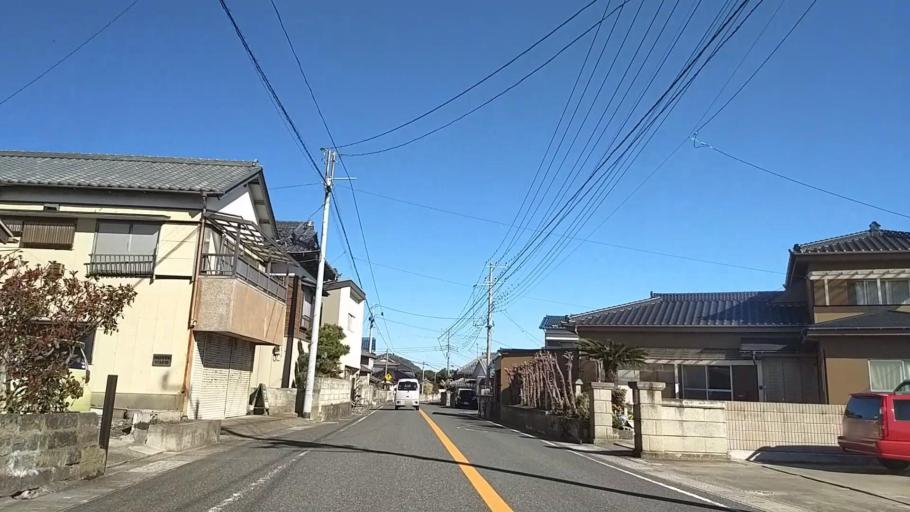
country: JP
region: Chiba
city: Tateyama
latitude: 34.9293
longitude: 139.9449
